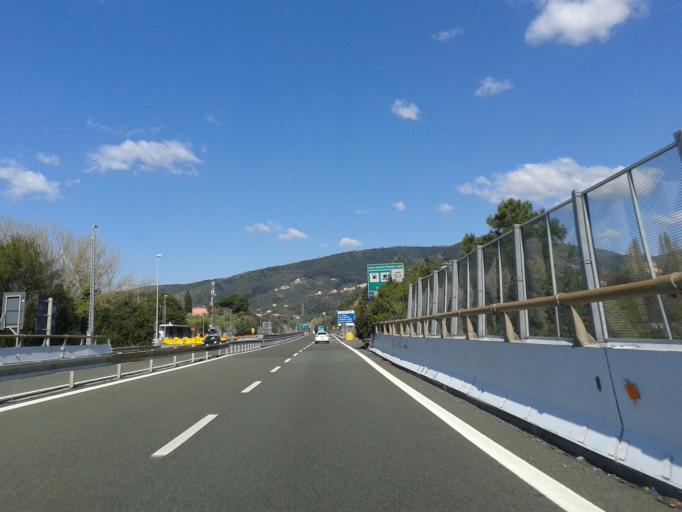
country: IT
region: Liguria
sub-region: Provincia di Genova
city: Casarza Ligure
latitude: 44.2704
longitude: 9.4260
